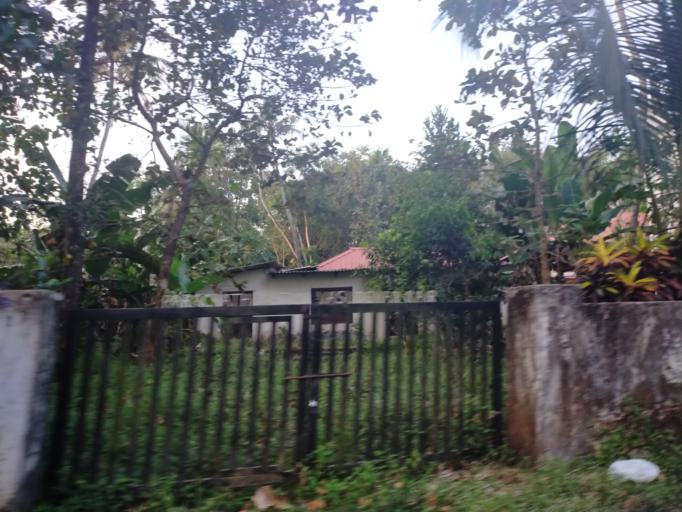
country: IN
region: Kerala
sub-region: Kottayam
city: Vaikam
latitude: 9.7370
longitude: 76.5117
